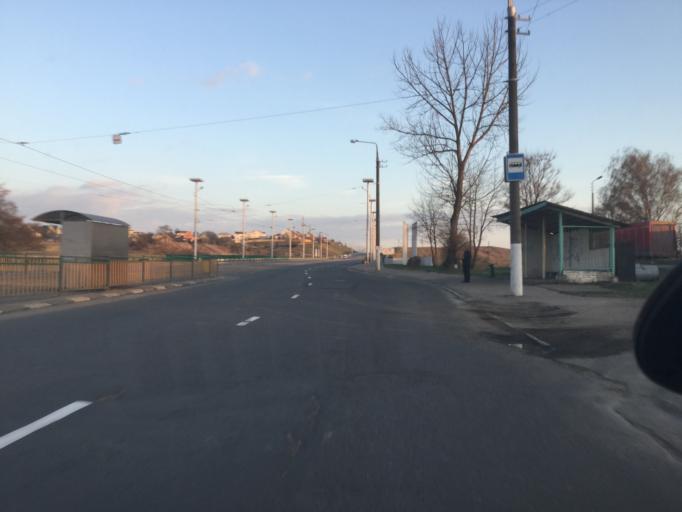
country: BY
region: Vitebsk
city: Vitebsk
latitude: 55.1711
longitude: 30.1660
